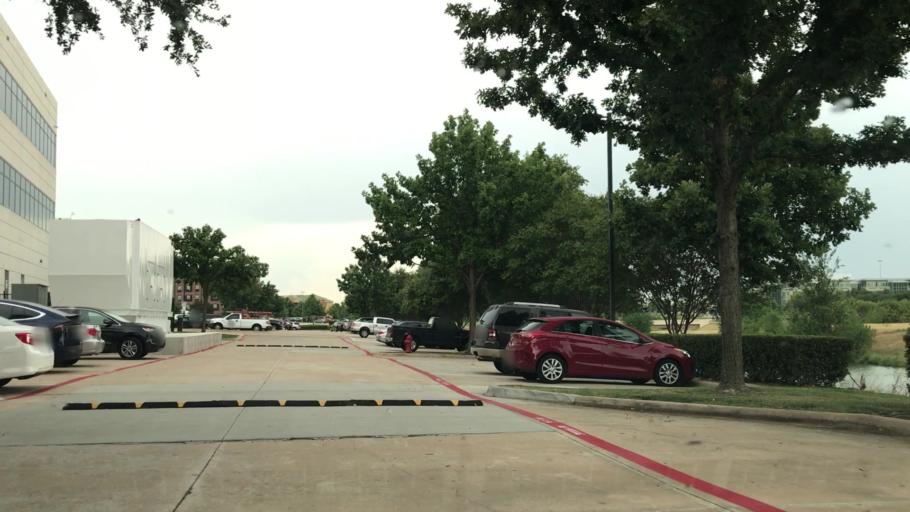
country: US
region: Texas
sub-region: Dallas County
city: Farmers Branch
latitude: 32.8988
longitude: -96.9653
